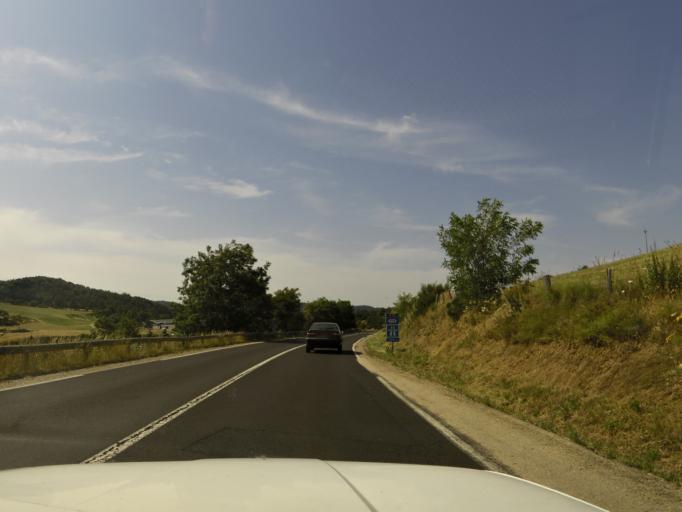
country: FR
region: Languedoc-Roussillon
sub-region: Departement de la Lozere
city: Marvejols
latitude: 44.5801
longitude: 3.2525
